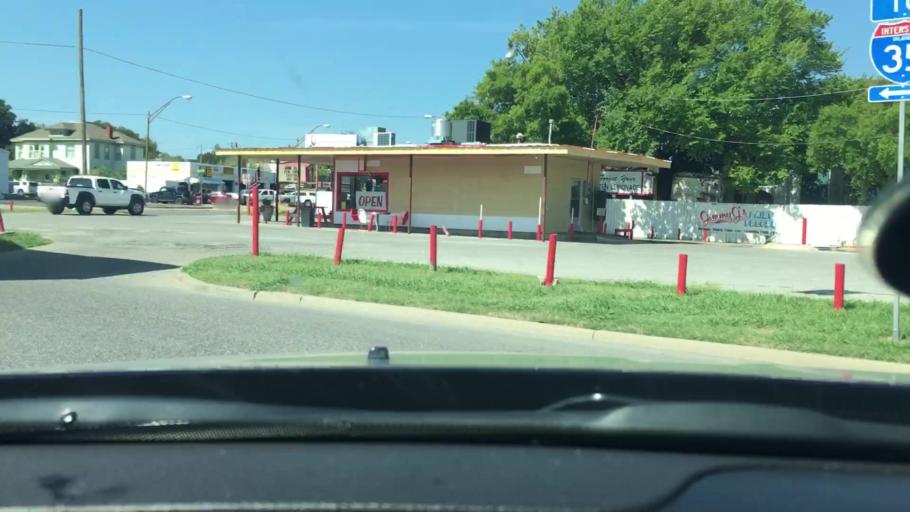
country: US
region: Oklahoma
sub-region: Carter County
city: Ardmore
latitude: 34.1749
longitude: -97.1360
